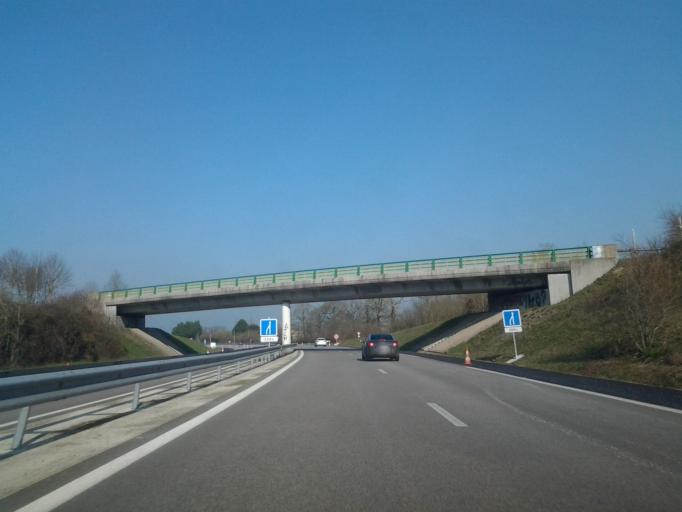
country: FR
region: Pays de la Loire
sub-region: Departement de la Vendee
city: Aizenay
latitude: 46.7461
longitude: -1.6224
